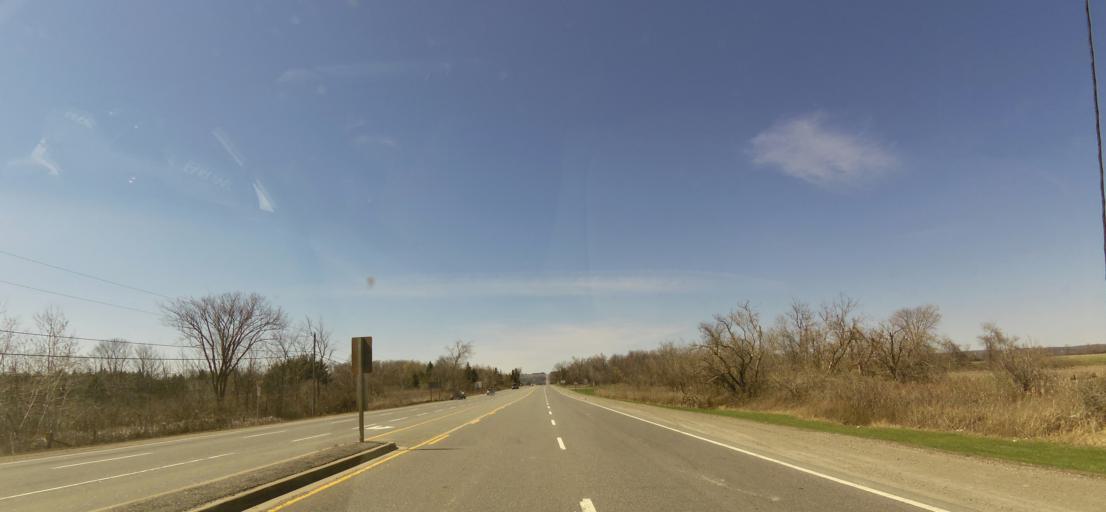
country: CA
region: Ontario
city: Brampton
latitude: 43.8011
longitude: -79.9157
